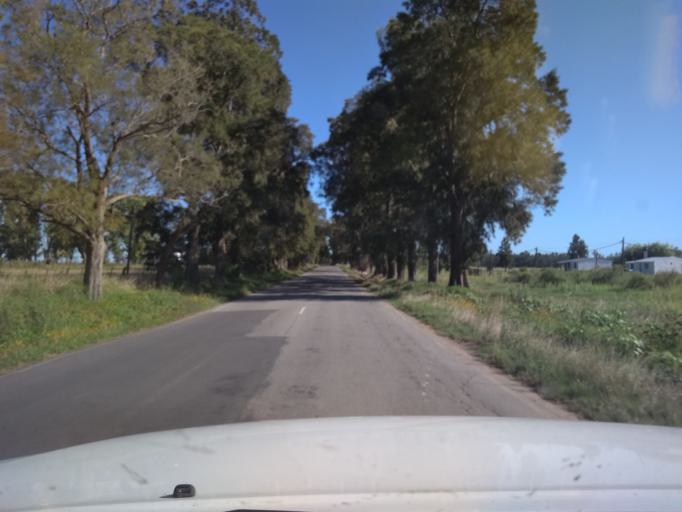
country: UY
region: Canelones
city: San Bautista
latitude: -34.3874
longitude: -55.9595
